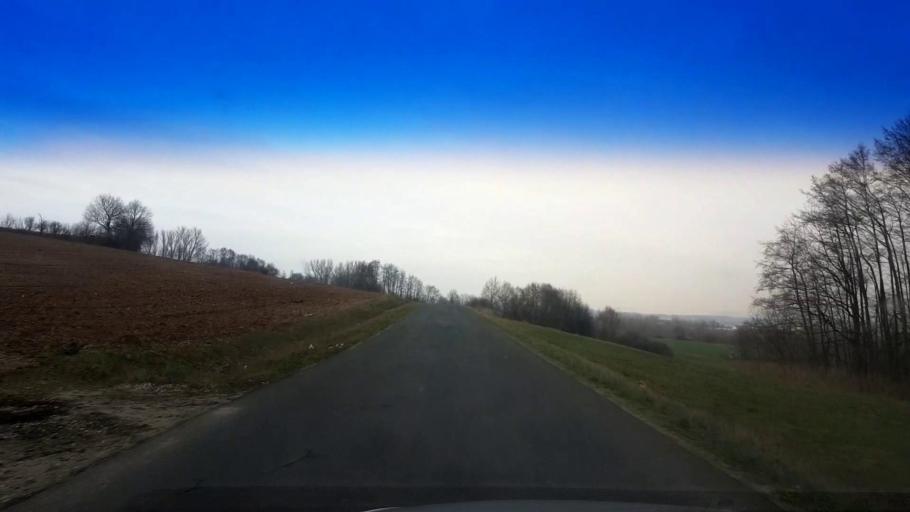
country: DE
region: Bavaria
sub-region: Upper Franconia
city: Hirschaid
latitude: 49.7972
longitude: 10.9939
